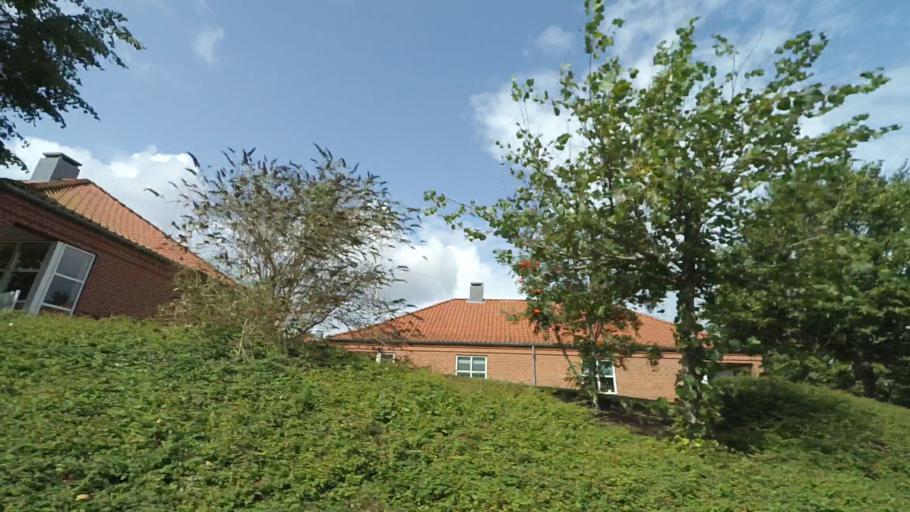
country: DK
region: Central Jutland
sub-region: Norddjurs Kommune
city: Allingabro
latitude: 56.4990
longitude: 10.3379
